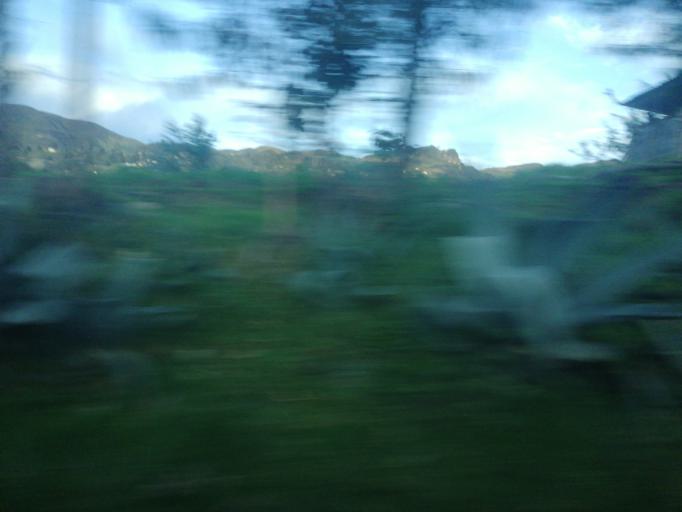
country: EC
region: Azuay
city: Nulti
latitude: -3.0324
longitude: -78.8021
